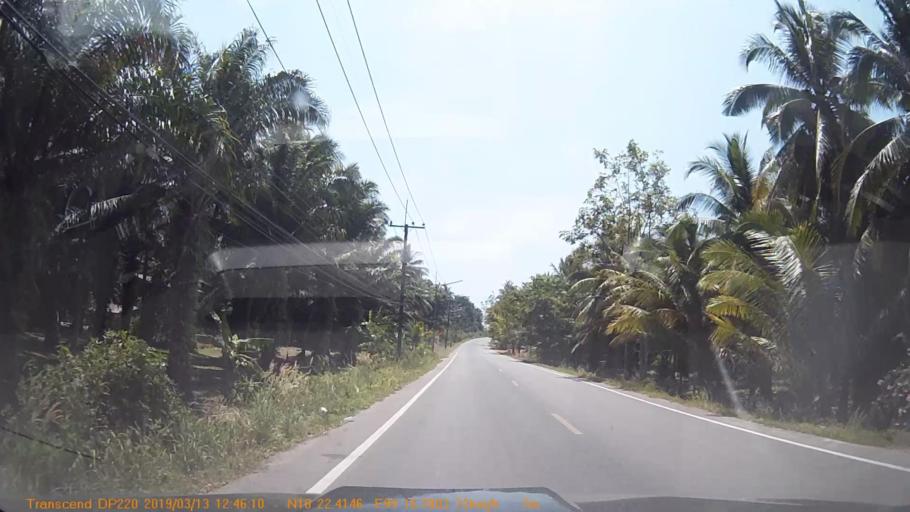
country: TH
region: Chumphon
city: Chumphon
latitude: 10.3731
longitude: 99.2630
